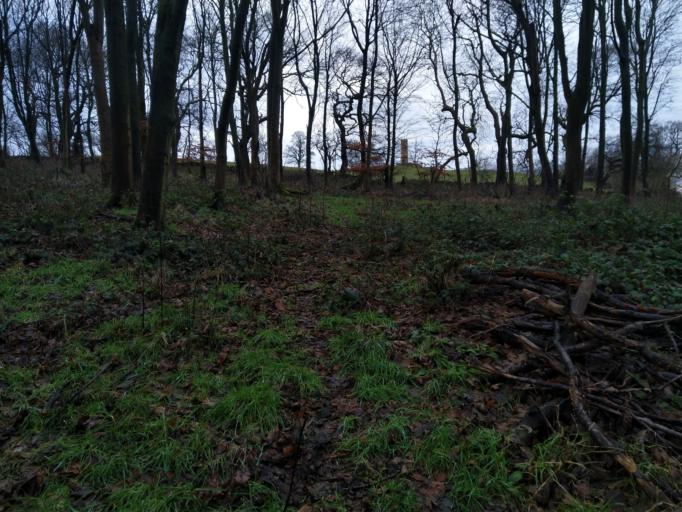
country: GB
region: Scotland
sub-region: Fife
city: Limekilns
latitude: 55.9921
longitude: -3.5164
